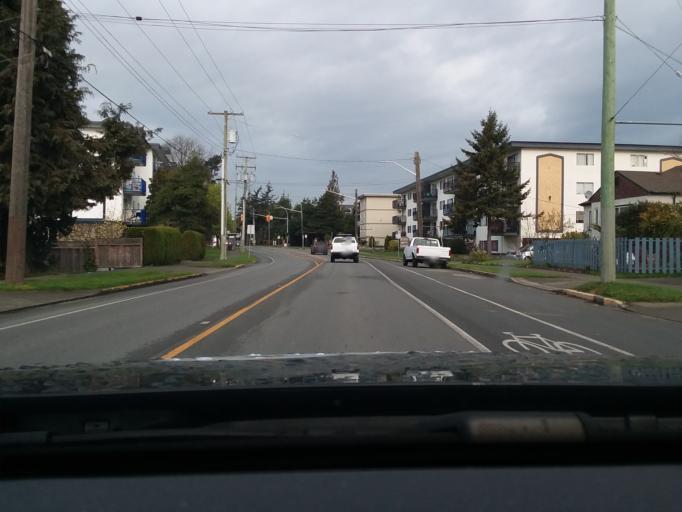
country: CA
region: British Columbia
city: Victoria
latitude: 48.4399
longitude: -123.3942
